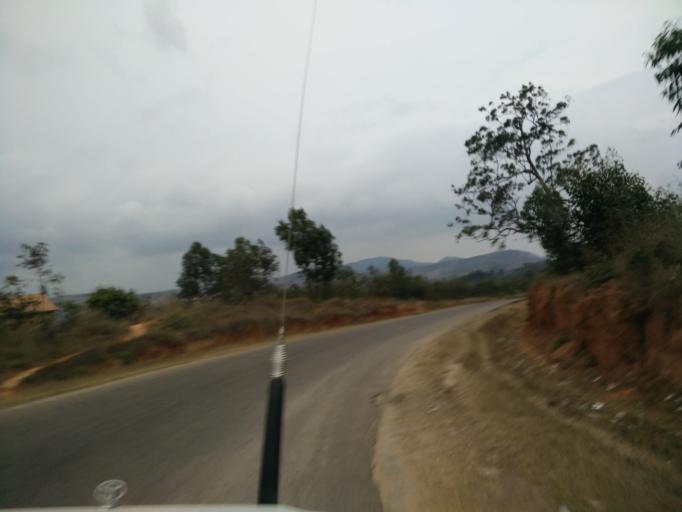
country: MG
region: Upper Matsiatra
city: Fianarantsoa
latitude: -21.5303
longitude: 47.0467
